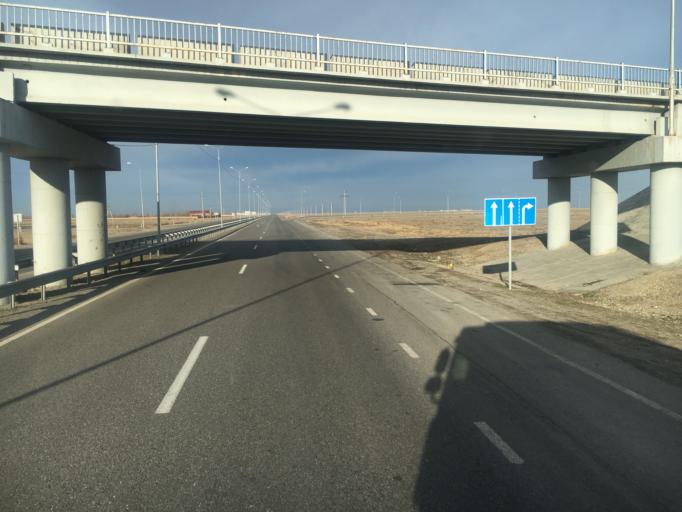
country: KZ
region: Ongtustik Qazaqstan
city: Turkestan
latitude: 43.4146
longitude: 68.0256
